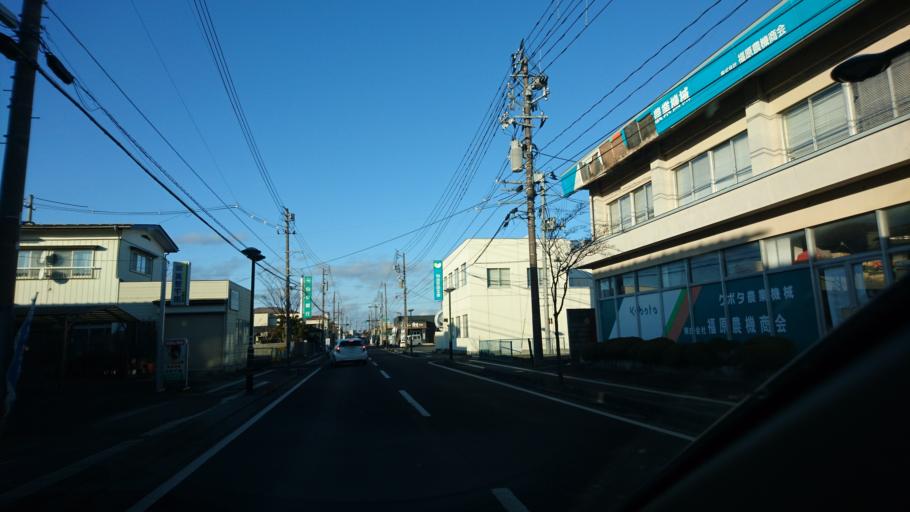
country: JP
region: Miyagi
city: Furukawa
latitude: 38.5685
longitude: 140.8594
